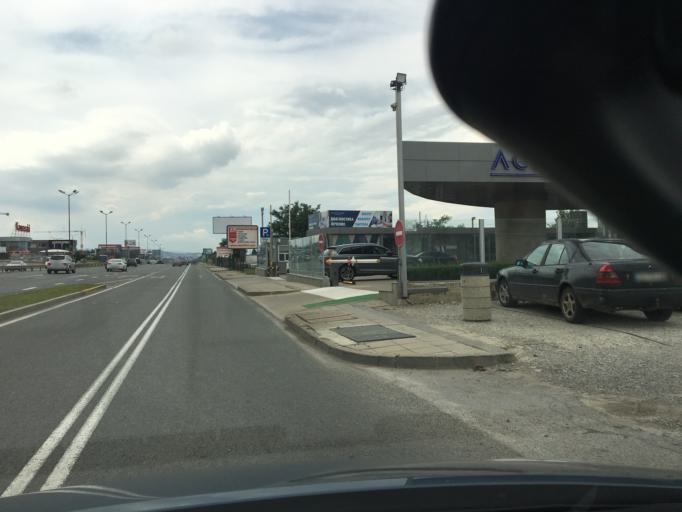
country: BG
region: Sofia-Capital
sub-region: Stolichna Obshtina
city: Sofia
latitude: 42.6395
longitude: 23.3182
